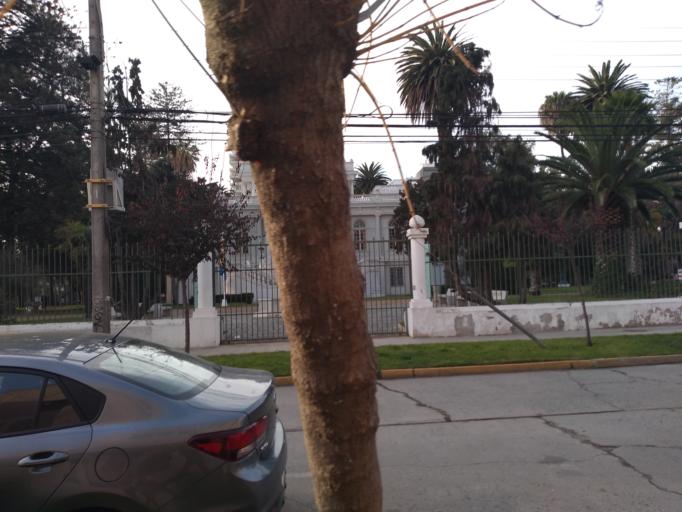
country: CL
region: Valparaiso
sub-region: Provincia de Valparaiso
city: Vina del Mar
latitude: -33.0211
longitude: -71.5467
